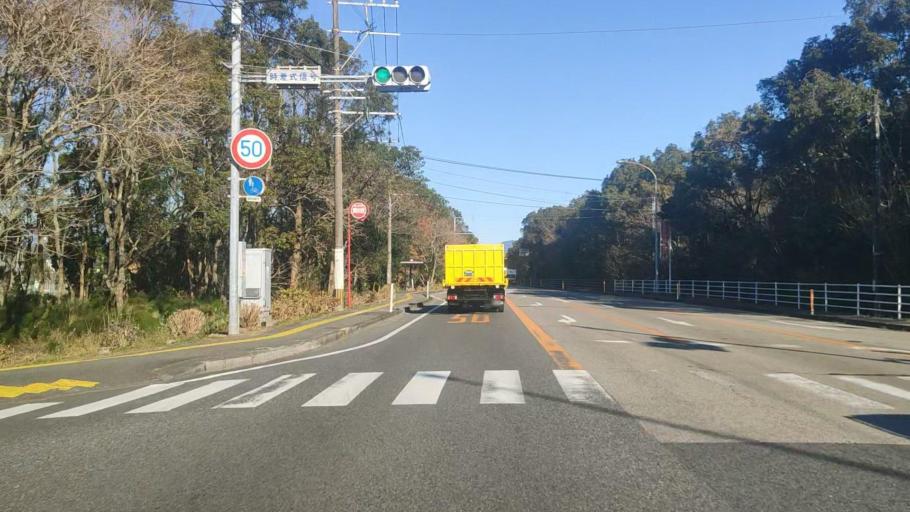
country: JP
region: Miyazaki
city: Nobeoka
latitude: 32.5290
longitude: 131.6817
